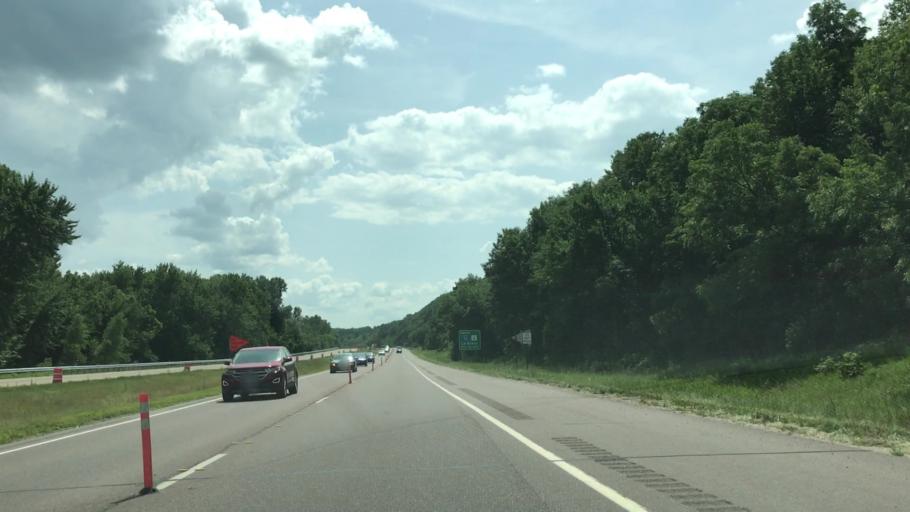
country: US
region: Minnesota
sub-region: Le Sueur County
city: Le Sueur
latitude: 44.4744
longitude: -93.9245
